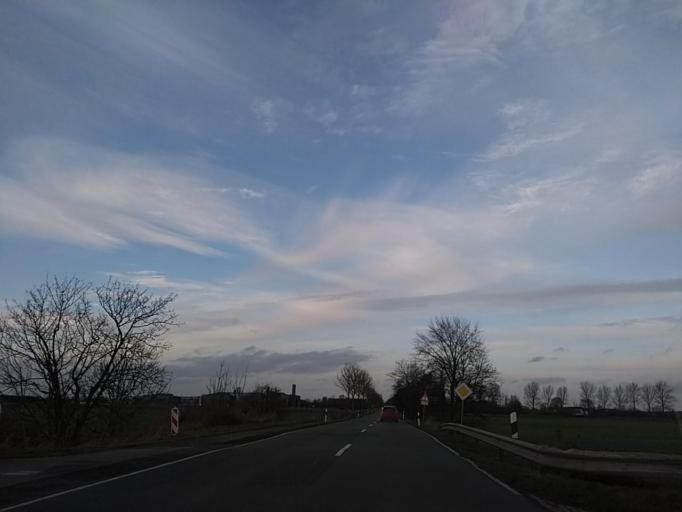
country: DE
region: Lower Saxony
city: Jemgum
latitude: 53.2444
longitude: 7.3907
